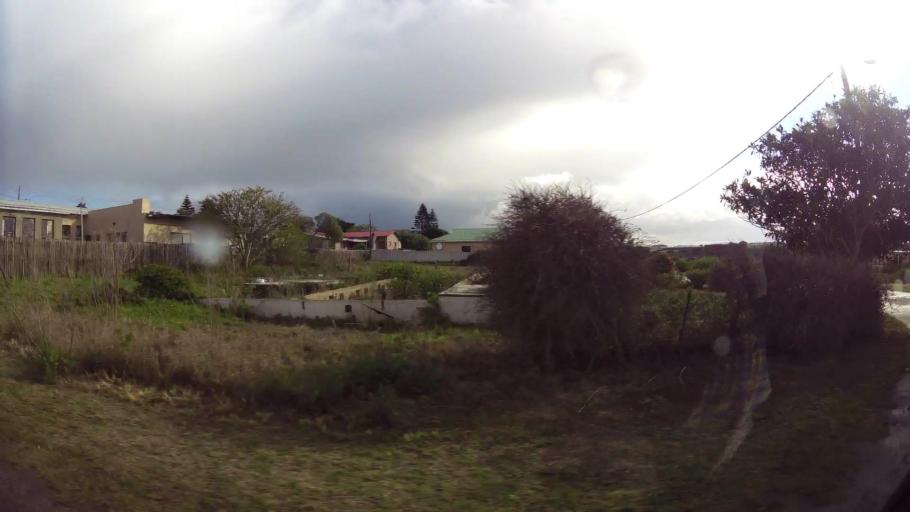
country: ZA
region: Western Cape
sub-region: Eden District Municipality
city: Mossel Bay
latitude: -34.1862
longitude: 22.1227
